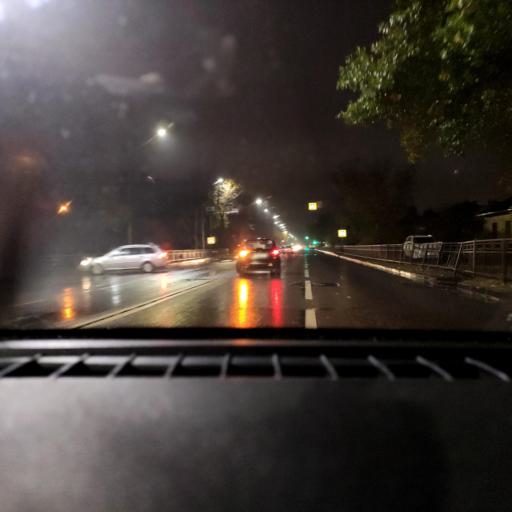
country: RU
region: Voronezj
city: Somovo
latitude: 51.7135
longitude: 39.2753
